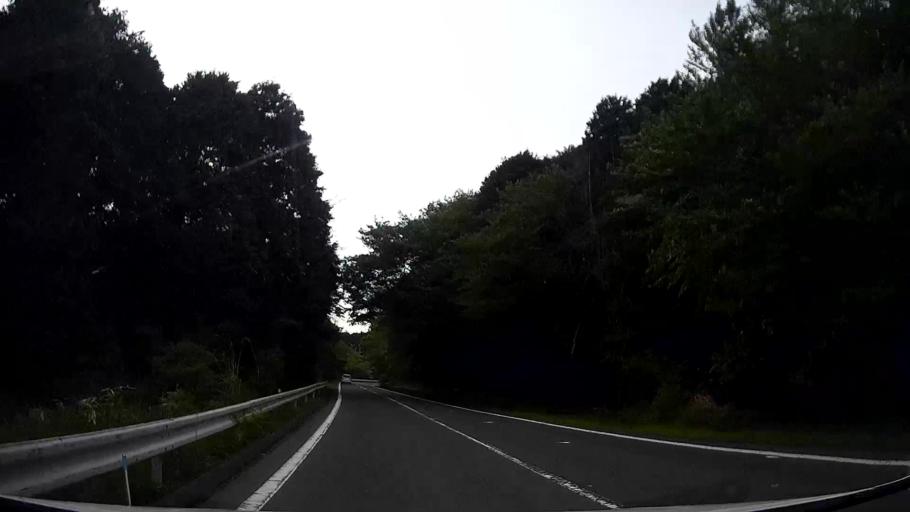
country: JP
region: Shizuoka
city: Ito
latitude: 35.0171
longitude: 139.0451
